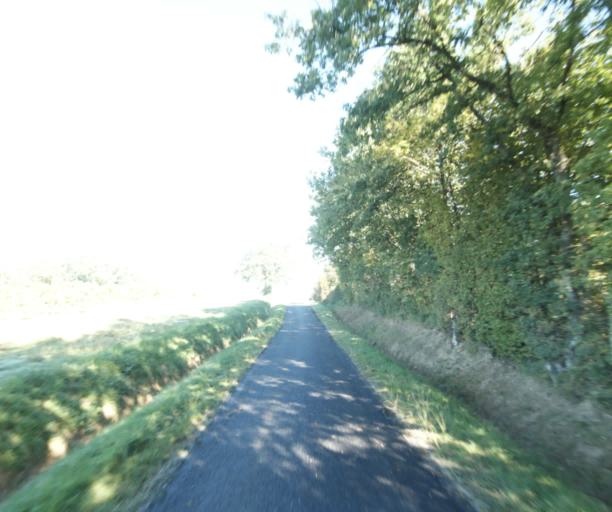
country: FR
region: Midi-Pyrenees
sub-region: Departement du Gers
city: Gondrin
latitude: 43.8136
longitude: 0.1950
